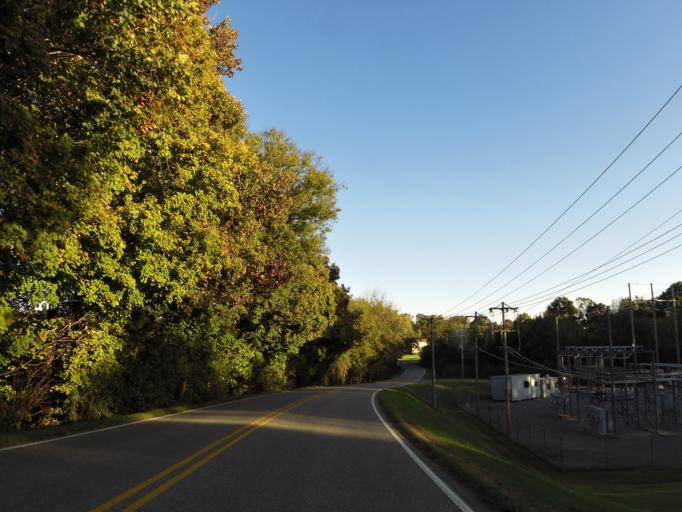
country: US
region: Tennessee
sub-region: Blount County
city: Eagleton Village
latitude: 35.8314
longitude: -83.9532
